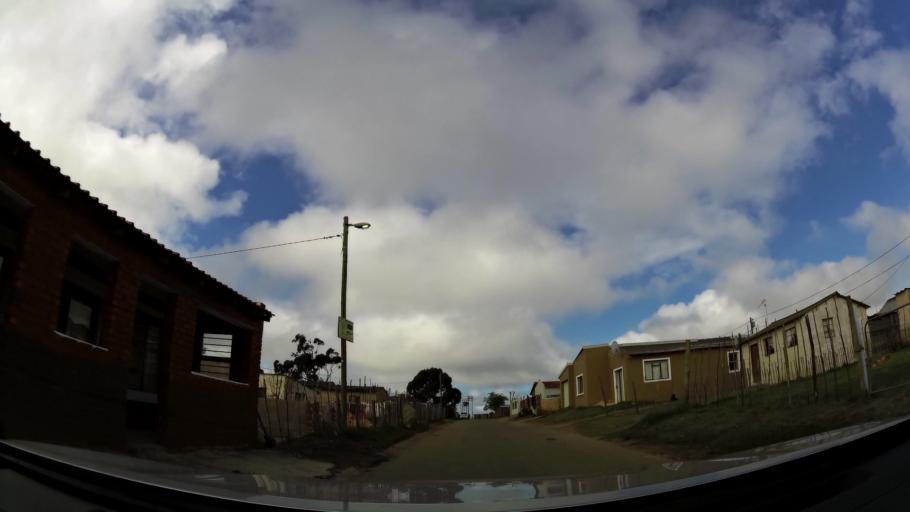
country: ZA
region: Western Cape
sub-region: Eden District Municipality
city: Plettenberg Bay
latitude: -34.0469
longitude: 23.3243
